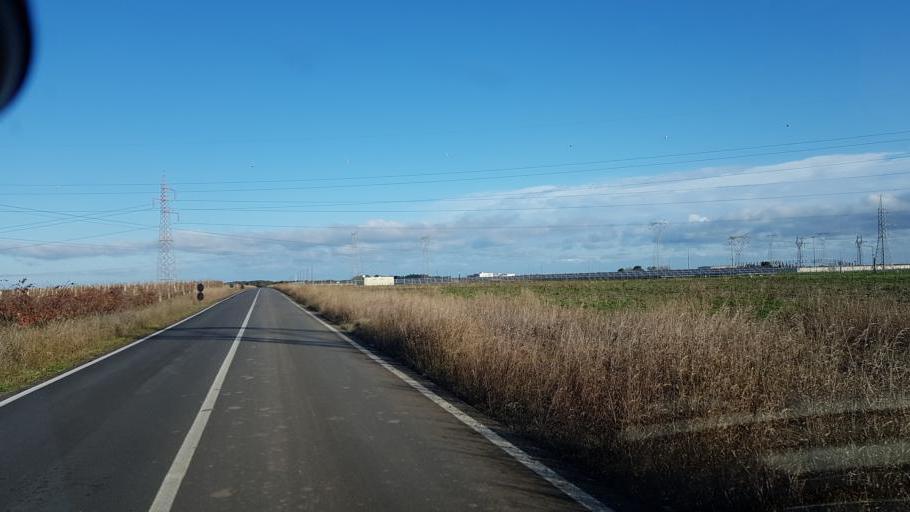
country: IT
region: Apulia
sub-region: Provincia di Brindisi
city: Tuturano
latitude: 40.5541
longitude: 17.9470
